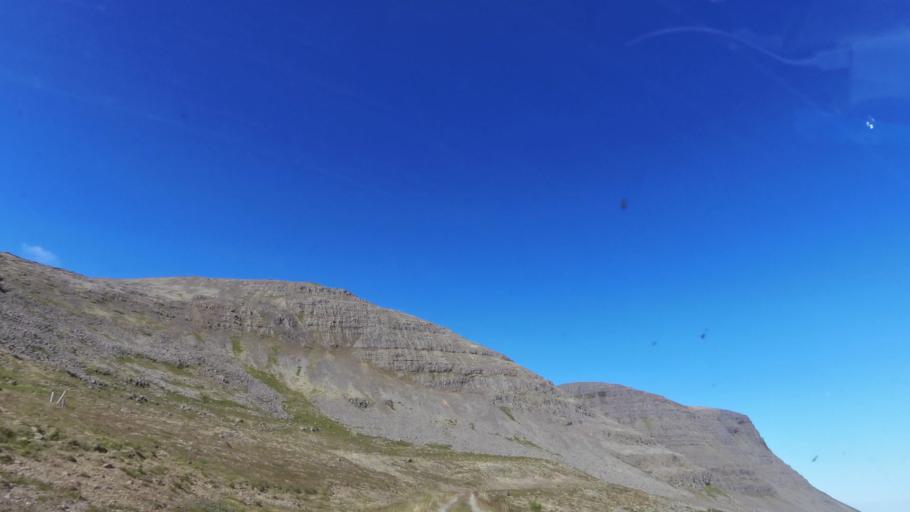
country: IS
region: West
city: Olafsvik
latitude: 65.6223
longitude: -23.8771
